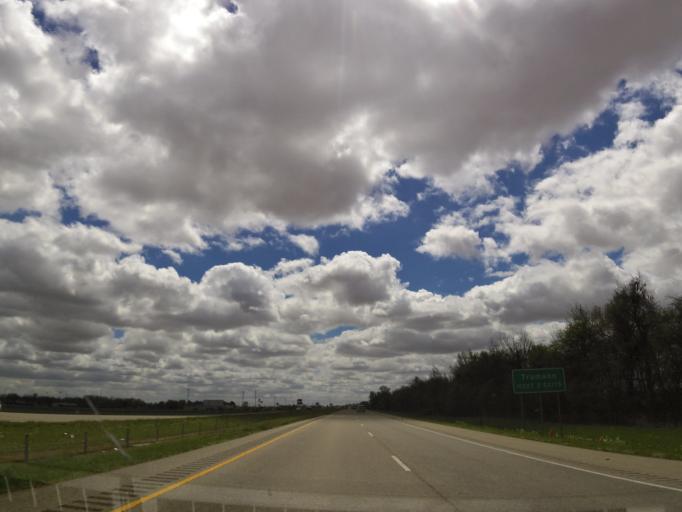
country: US
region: Arkansas
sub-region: Poinsett County
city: Trumann
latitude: 35.6907
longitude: -90.5528
